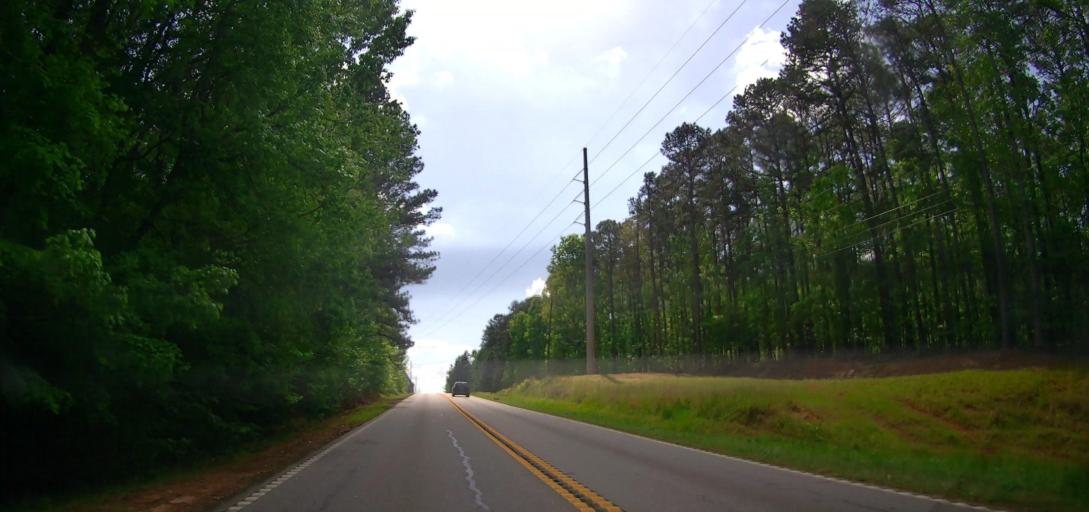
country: US
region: Georgia
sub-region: Putnam County
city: Jefferson
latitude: 33.4859
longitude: -83.2312
